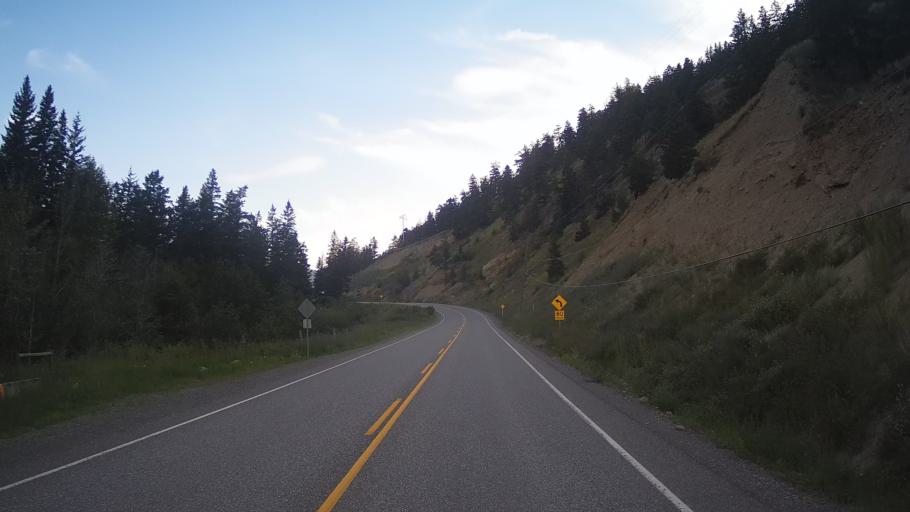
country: CA
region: British Columbia
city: Cache Creek
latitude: 50.8674
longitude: -121.5250
